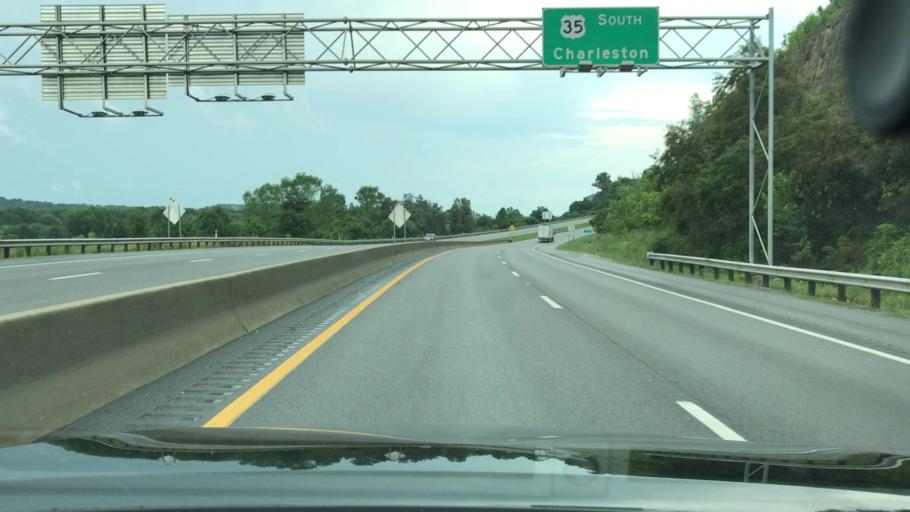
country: US
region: West Virginia
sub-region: Mason County
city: Point Pleasant
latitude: 38.8295
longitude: -82.1338
